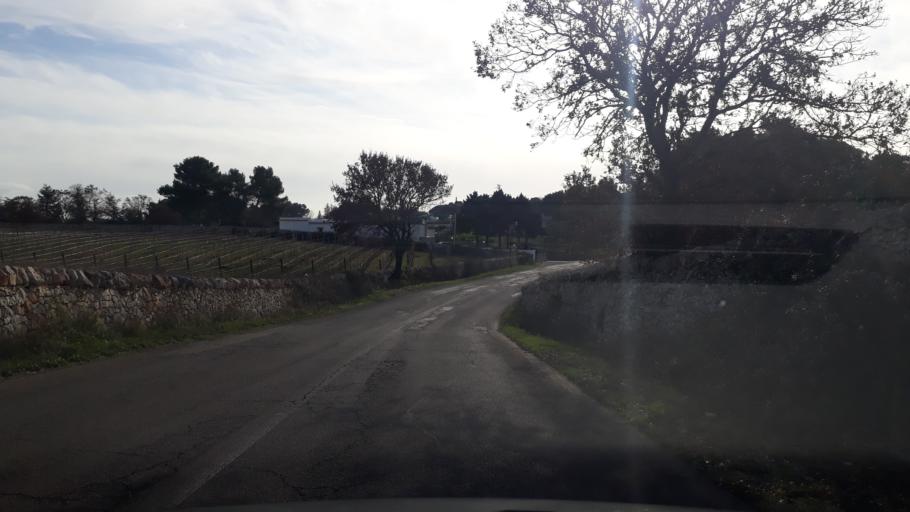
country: IT
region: Apulia
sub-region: Provincia di Taranto
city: Martina Franca
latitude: 40.6753
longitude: 17.3621
